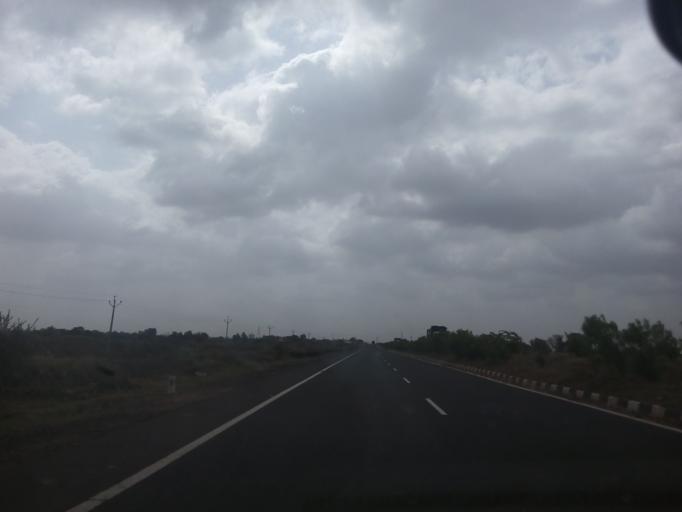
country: IN
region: Gujarat
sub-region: Surendranagar
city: Halvad
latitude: 23.0220
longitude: 70.9896
